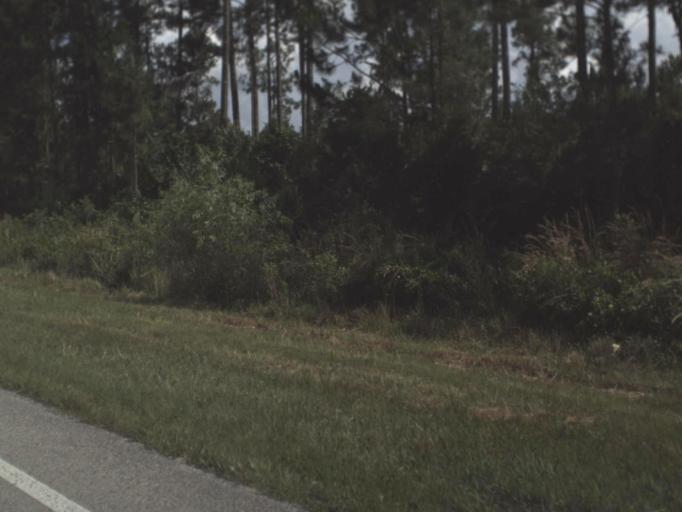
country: US
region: Florida
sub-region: Alachua County
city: Alachua
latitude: 29.7288
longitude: -82.3738
